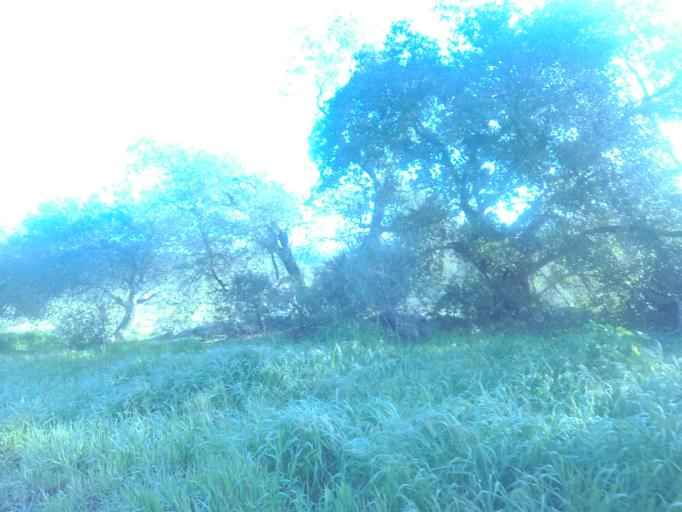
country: US
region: California
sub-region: Riverside County
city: Corona
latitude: 33.8021
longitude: -117.6552
